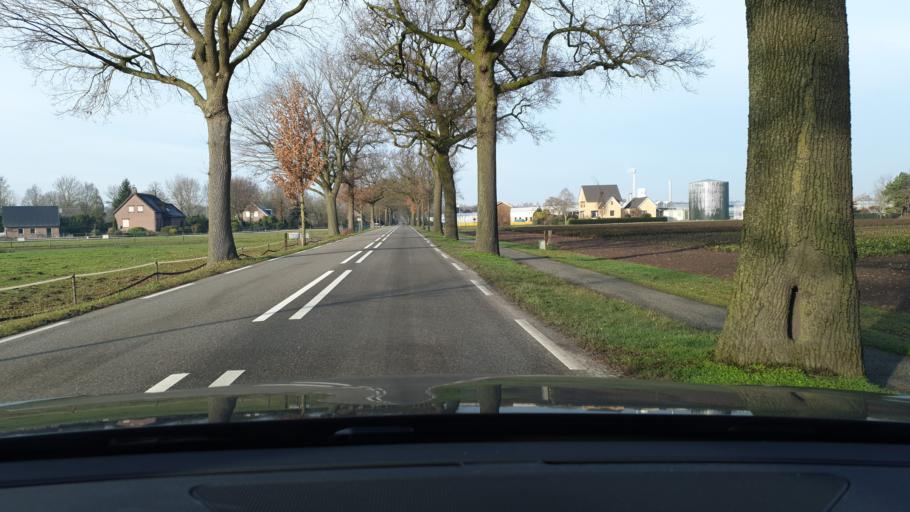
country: NL
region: Limburg
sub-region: Gemeente Peel en Maas
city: Maasbree
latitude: 51.4343
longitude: 6.0896
